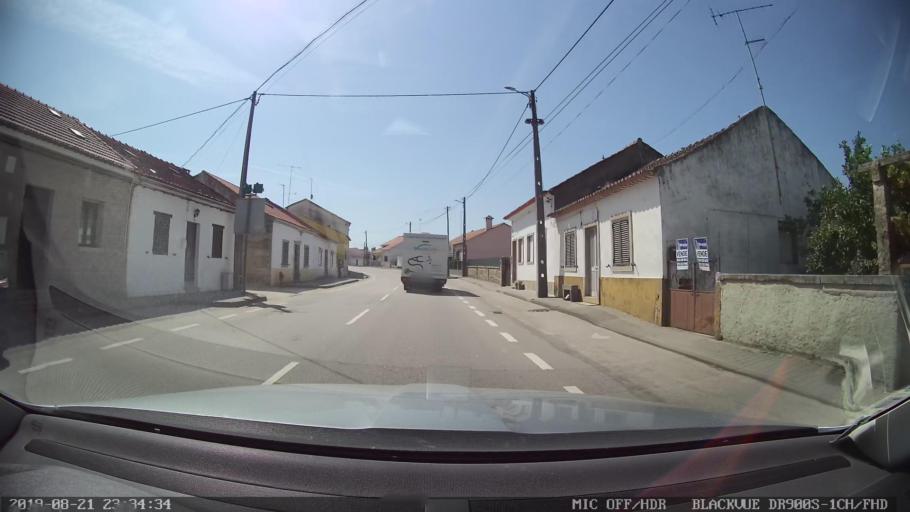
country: PT
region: Guarda
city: Alcains
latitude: 39.8807
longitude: -7.3964
